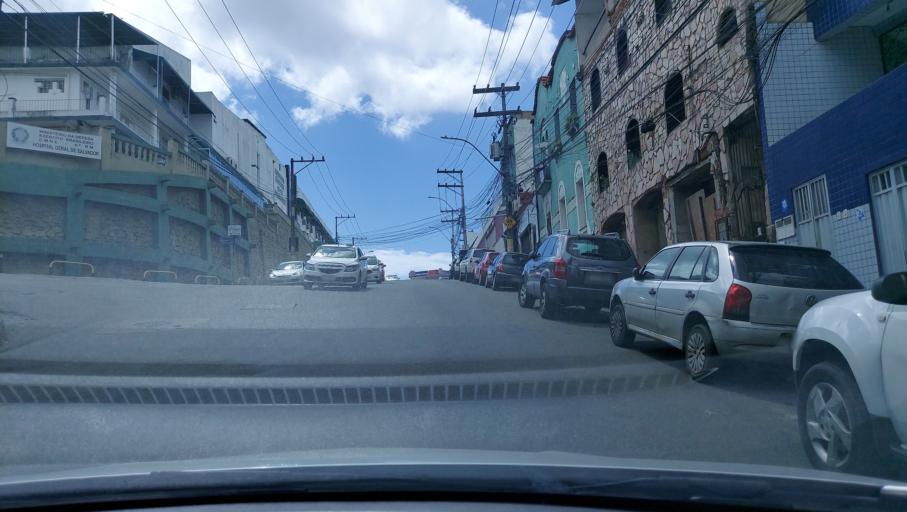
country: BR
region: Bahia
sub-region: Salvador
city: Salvador
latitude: -12.9772
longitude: -38.5004
